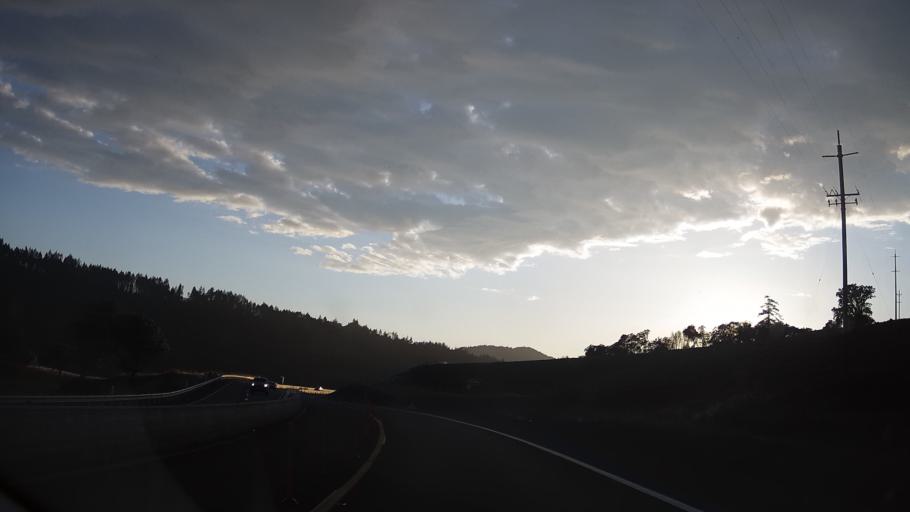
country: US
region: California
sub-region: Mendocino County
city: Redwood Valley
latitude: 39.3012
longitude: -123.2894
